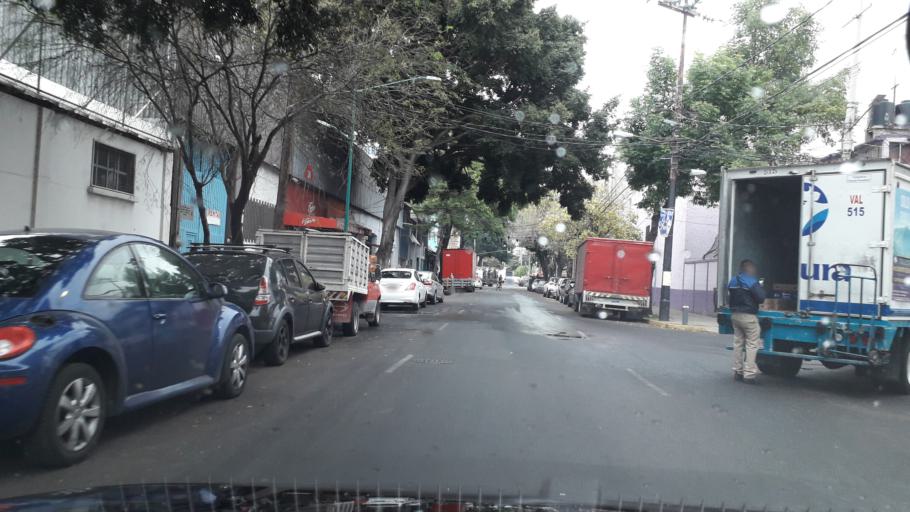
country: MX
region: Mexico City
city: Cuauhtemoc
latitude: 19.4575
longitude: -99.1572
